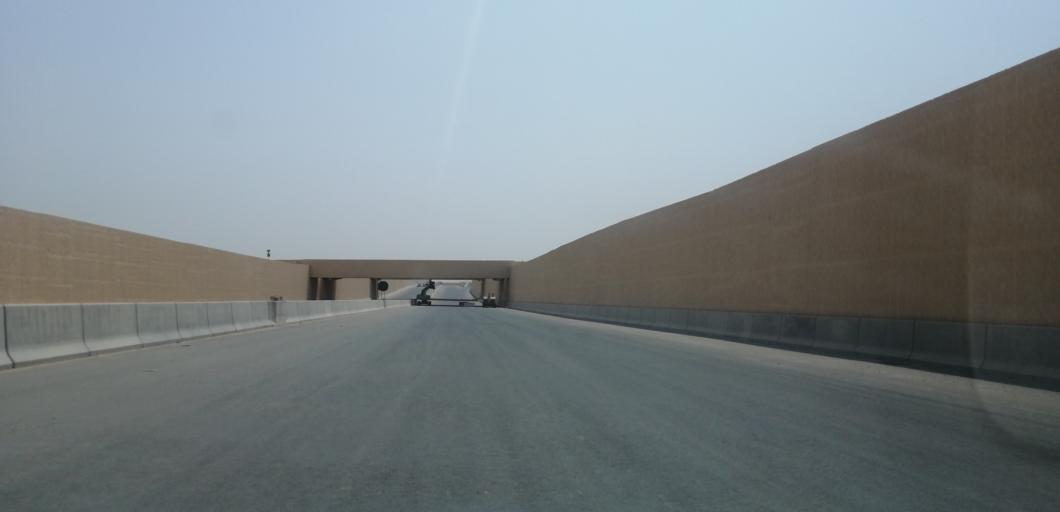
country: KW
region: Muhafazat al Jahra'
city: Al Jahra'
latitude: 29.4532
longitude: 47.5771
